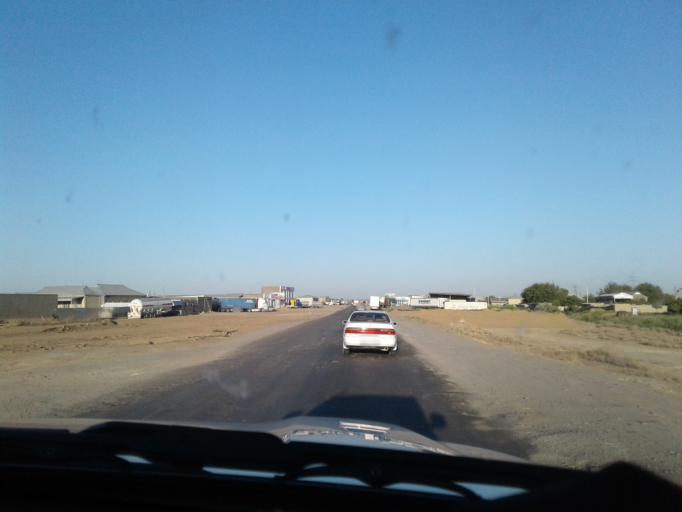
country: TM
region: Mary
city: Mary
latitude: 37.5663
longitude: 61.8130
